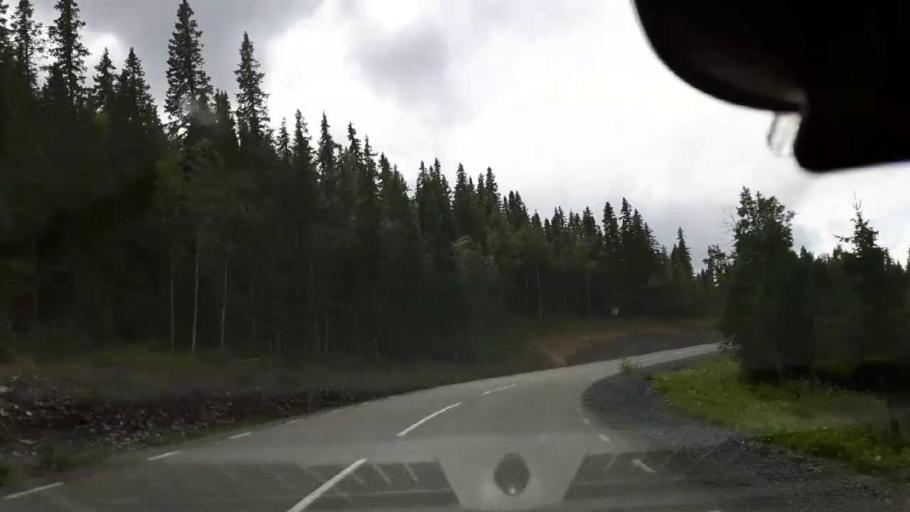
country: SE
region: Jaemtland
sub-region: Krokoms Kommun
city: Valla
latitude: 63.4860
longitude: 13.8605
